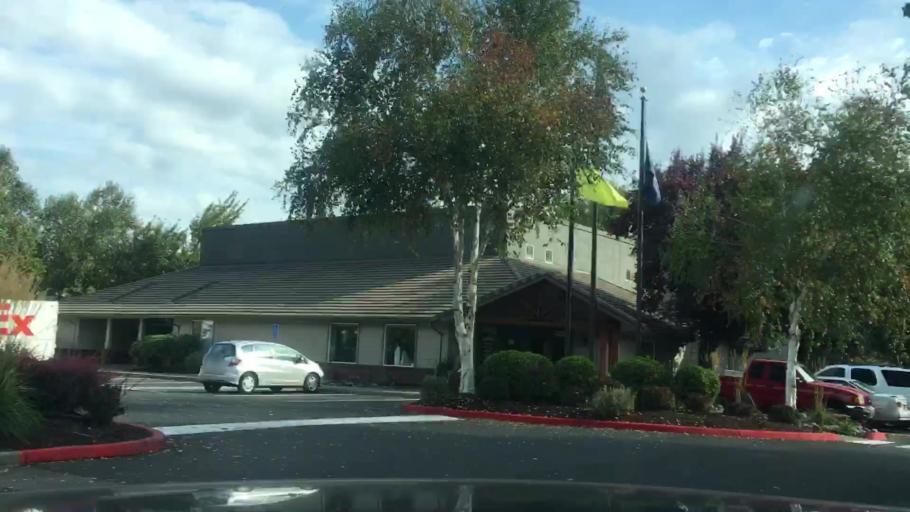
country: US
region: Oregon
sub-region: Lane County
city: Eugene
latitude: 44.0839
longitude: -123.1098
